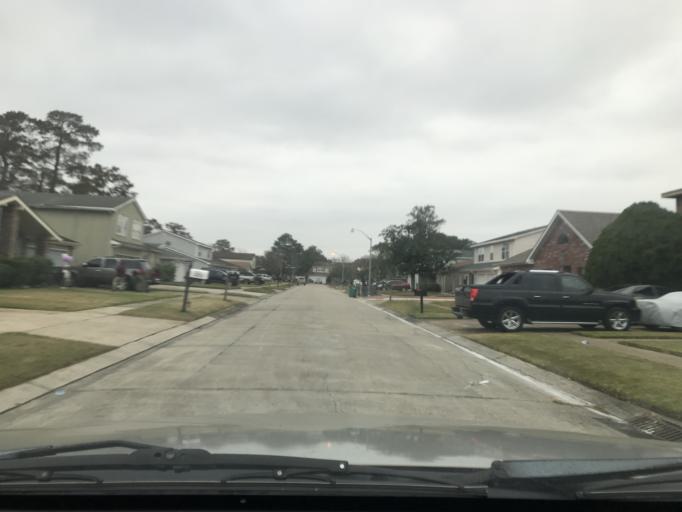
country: US
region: Louisiana
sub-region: Jefferson Parish
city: Woodmere
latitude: 29.8627
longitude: -90.0770
